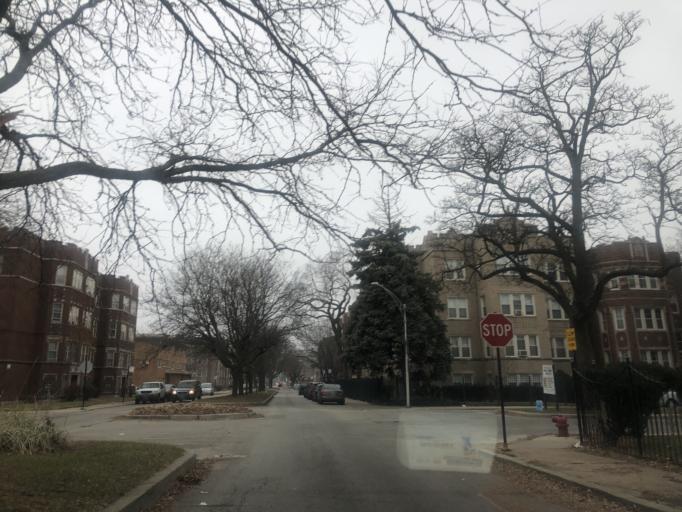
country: US
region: Illinois
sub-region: Cook County
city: Evergreen Park
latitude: 41.7475
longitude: -87.6120
